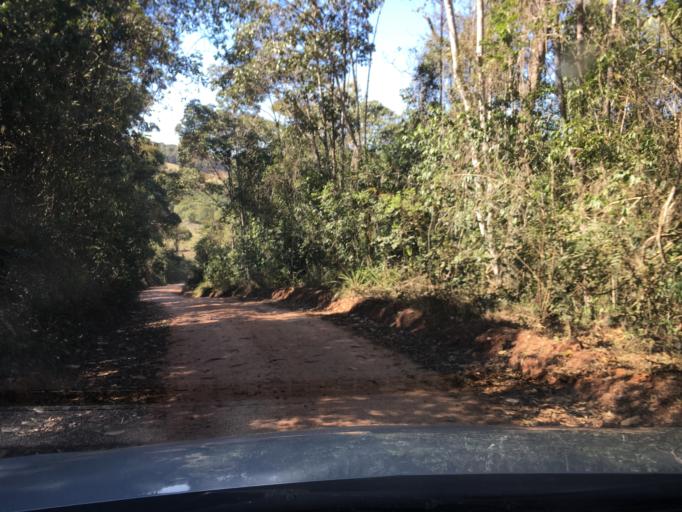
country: BR
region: Minas Gerais
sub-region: Campestre
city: Campestre
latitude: -21.5944
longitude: -46.2066
